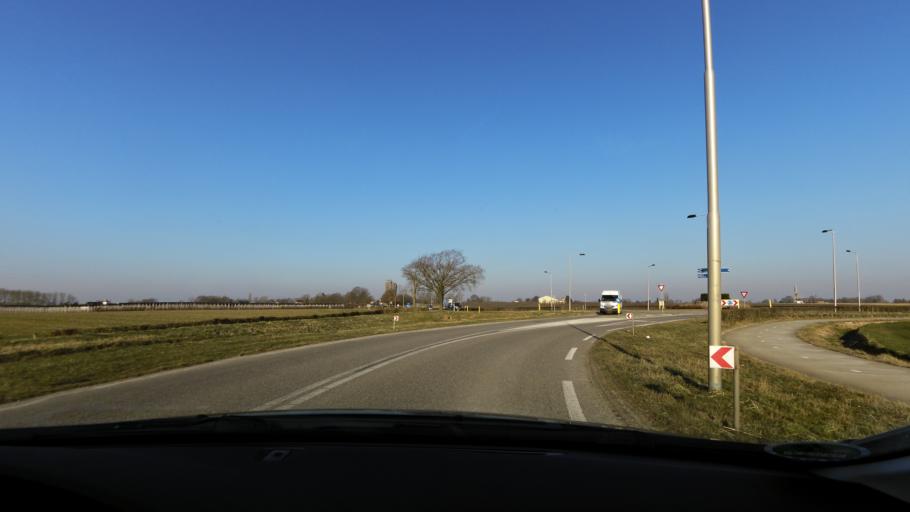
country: NL
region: Limburg
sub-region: Valkenburg aan de Geul
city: Broekhem
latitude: 50.8956
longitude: 5.8339
